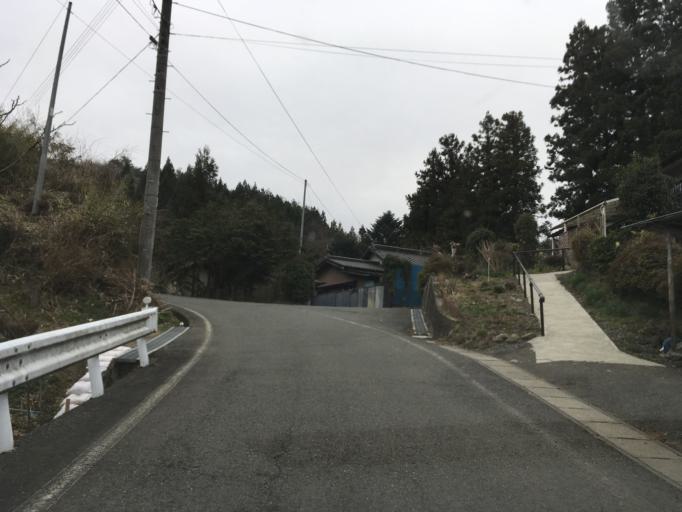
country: JP
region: Iwate
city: Ichinoseki
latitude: 38.7616
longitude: 141.2238
